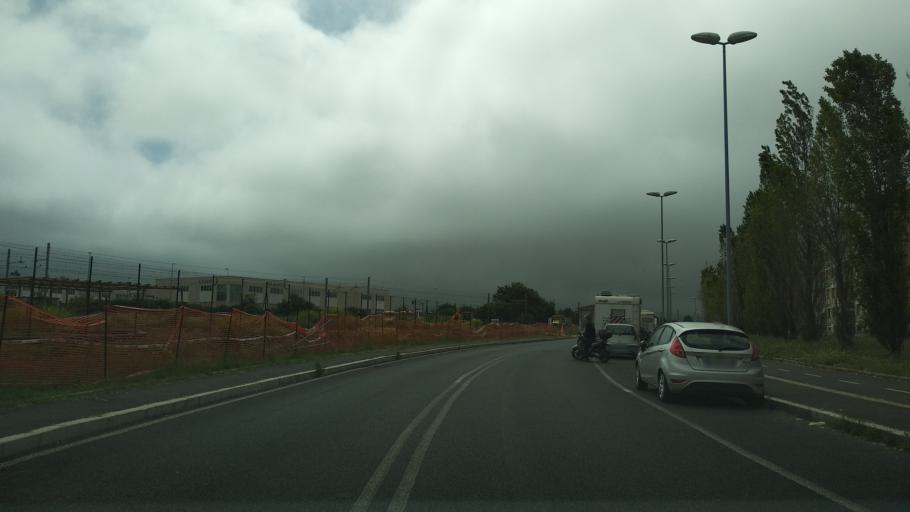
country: IT
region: Tuscany
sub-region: Provincia di Livorno
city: Livorno
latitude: 43.5382
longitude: 10.3323
